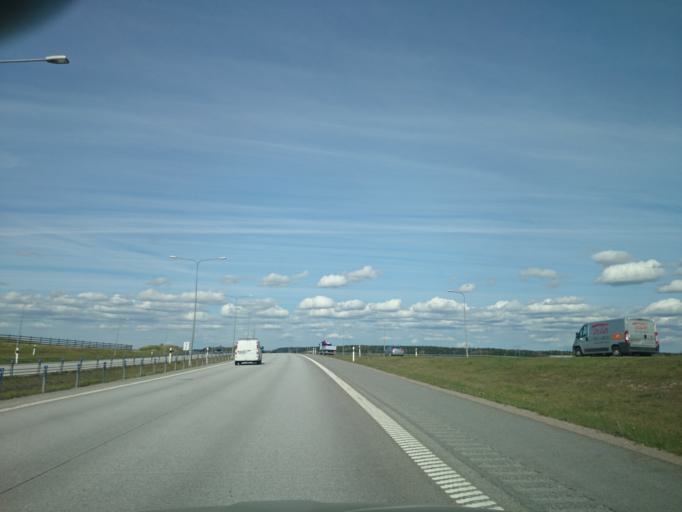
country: SE
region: Uppsala
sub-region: Uppsala Kommun
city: Saevja
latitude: 59.8462
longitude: 17.7343
